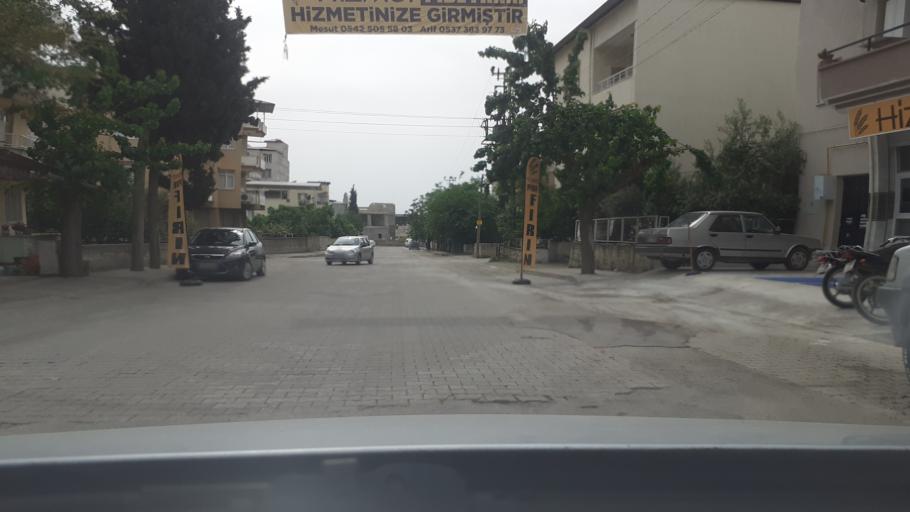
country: TR
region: Hatay
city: Kirikhan
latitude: 36.4945
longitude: 36.3654
